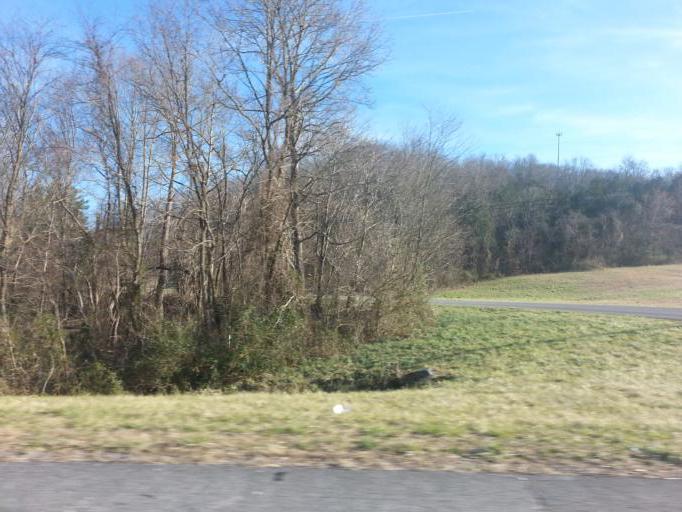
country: US
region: Tennessee
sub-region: Warren County
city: McMinnville
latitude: 35.7207
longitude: -85.6905
